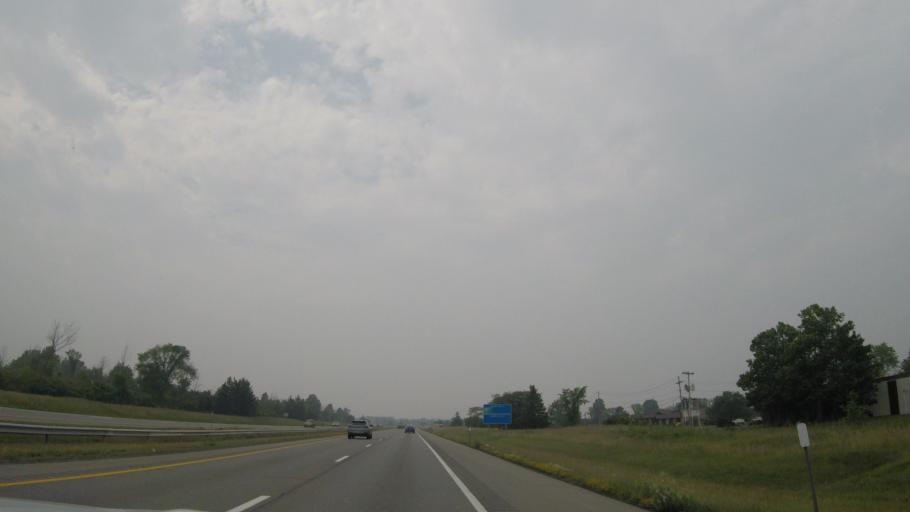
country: US
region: New York
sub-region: Erie County
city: Grandyle Village
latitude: 43.0390
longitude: -78.9860
